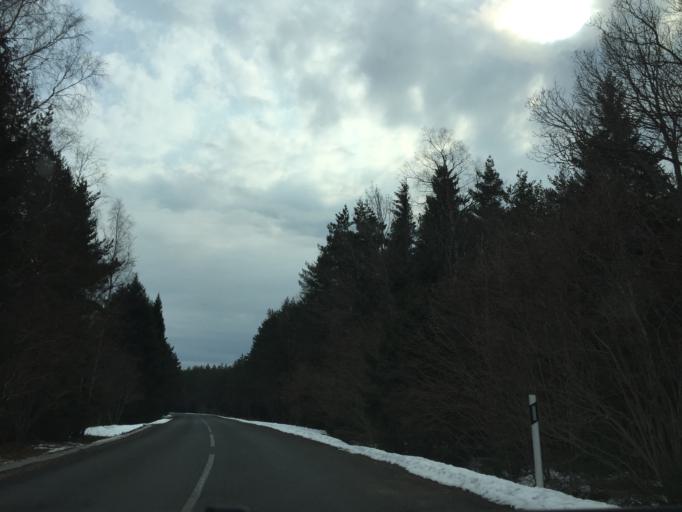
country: EE
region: Saare
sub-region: Kuressaare linn
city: Kuressaare
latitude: 58.4490
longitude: 22.0524
